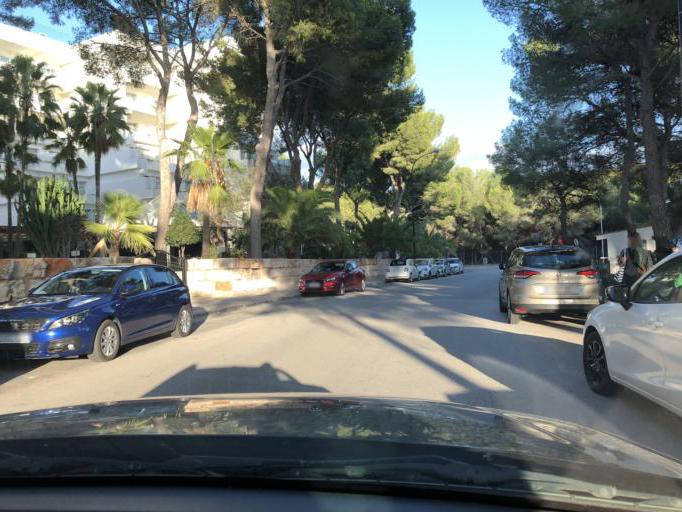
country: ES
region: Balearic Islands
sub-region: Illes Balears
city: Santa Ponsa
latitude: 39.5343
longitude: 2.4602
